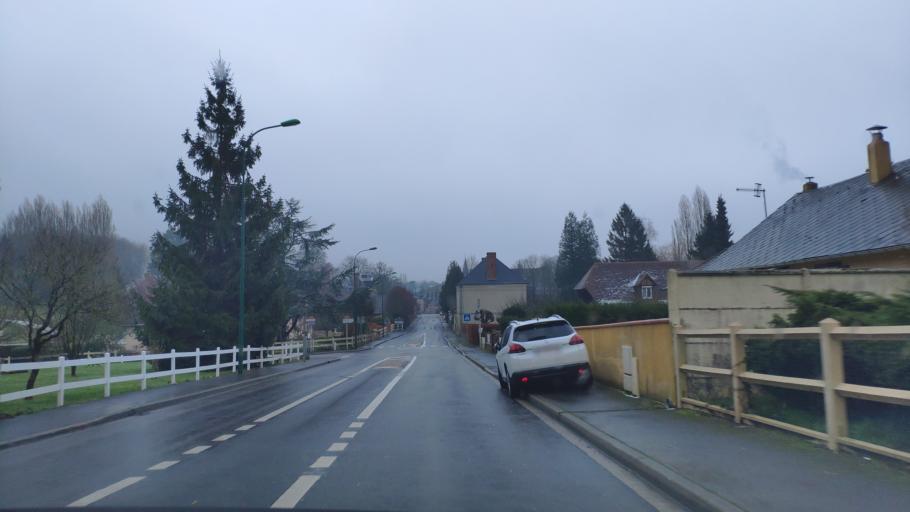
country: FR
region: Haute-Normandie
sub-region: Departement de la Seine-Maritime
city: Doudeville
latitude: 49.7200
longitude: 0.7758
